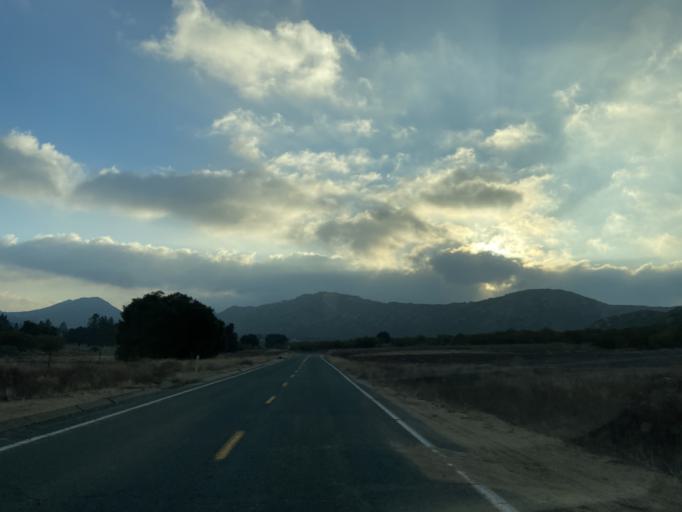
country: US
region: California
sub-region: San Diego County
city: Pine Valley
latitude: 32.7236
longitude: -116.4658
